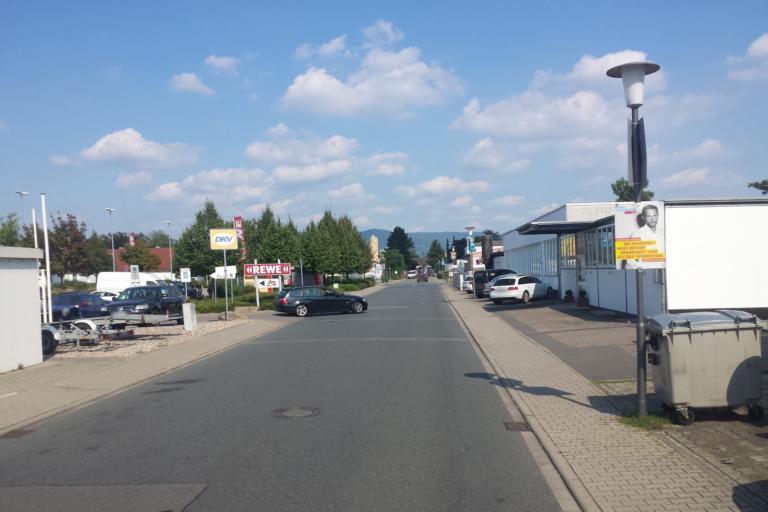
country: DE
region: Baden-Wuerttemberg
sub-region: Karlsruhe Region
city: Eppelheim
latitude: 49.4087
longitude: 8.6284
